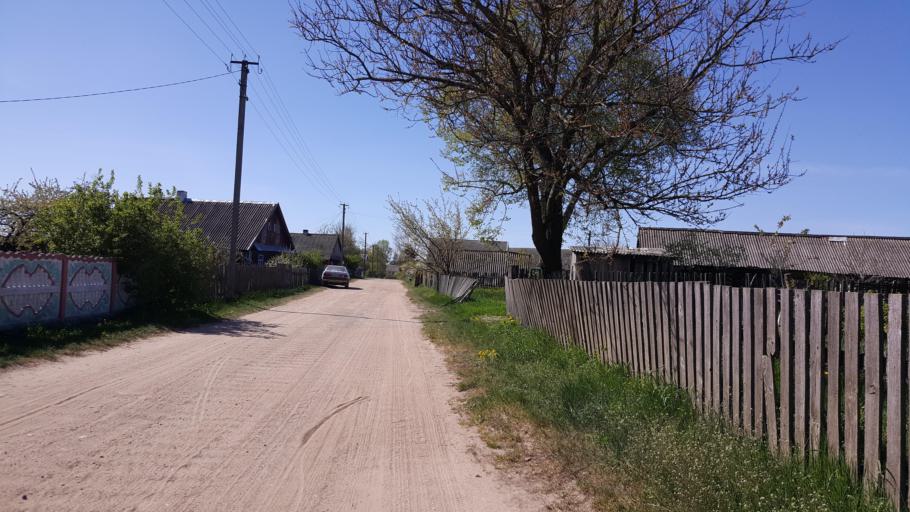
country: BY
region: Brest
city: Kamyanyets
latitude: 52.4544
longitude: 23.8823
